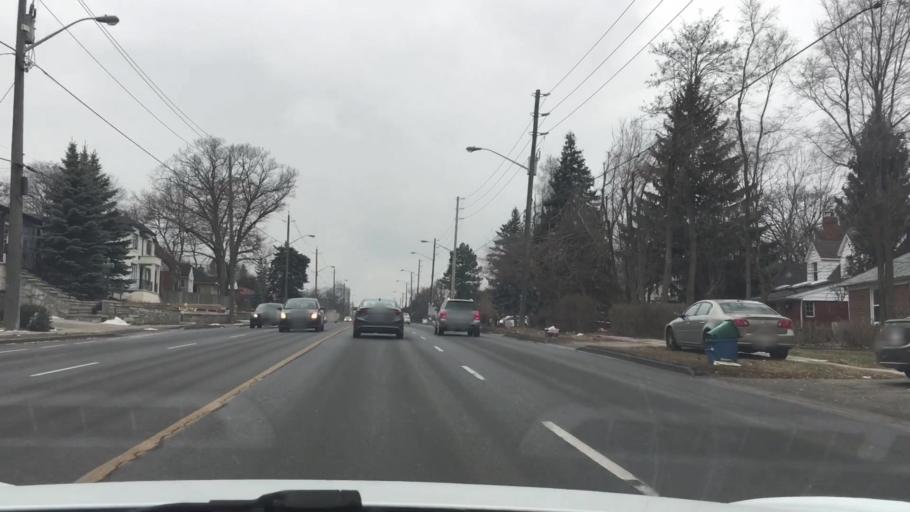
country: CA
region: Ontario
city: North York
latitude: 43.8004
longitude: -79.4096
